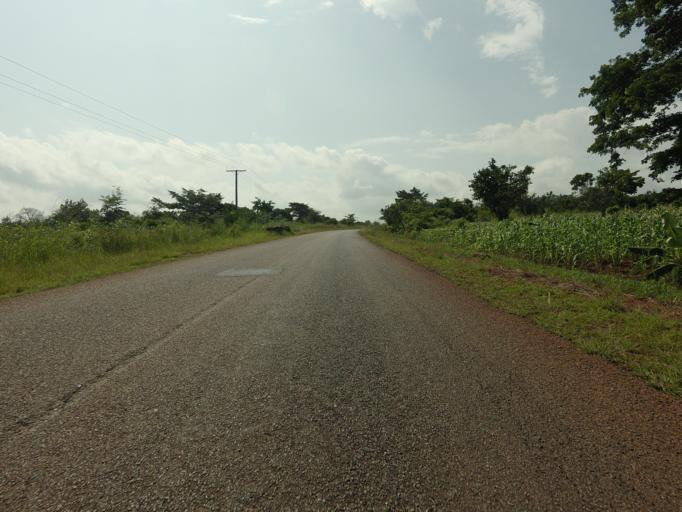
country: TG
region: Maritime
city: Tsevie
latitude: 6.3419
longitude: 0.8736
